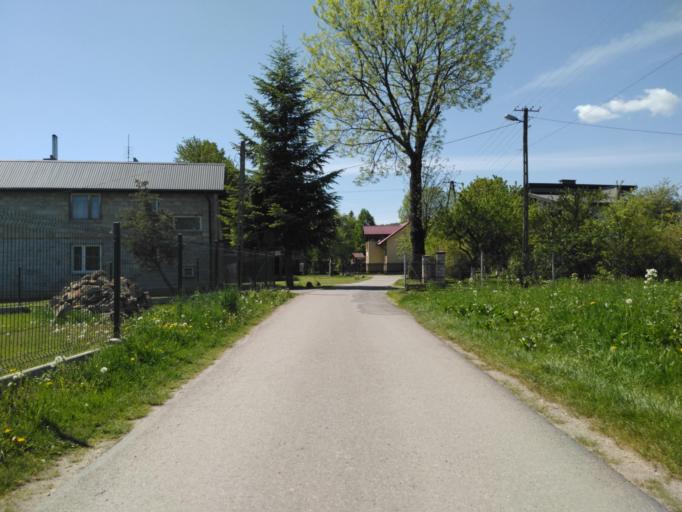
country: PL
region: Subcarpathian Voivodeship
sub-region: Powiat krosnienski
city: Miejsce Piastowe
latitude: 49.5995
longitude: 21.7980
